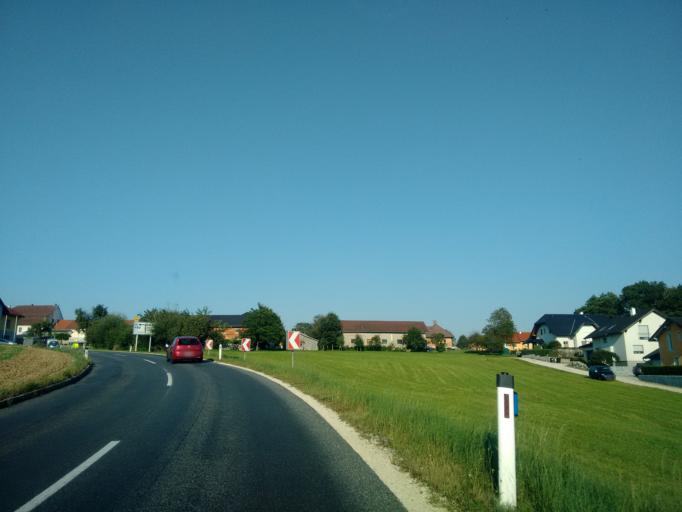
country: AT
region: Upper Austria
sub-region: Wels-Land
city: Sattledt
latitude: 48.0090
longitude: 14.0598
